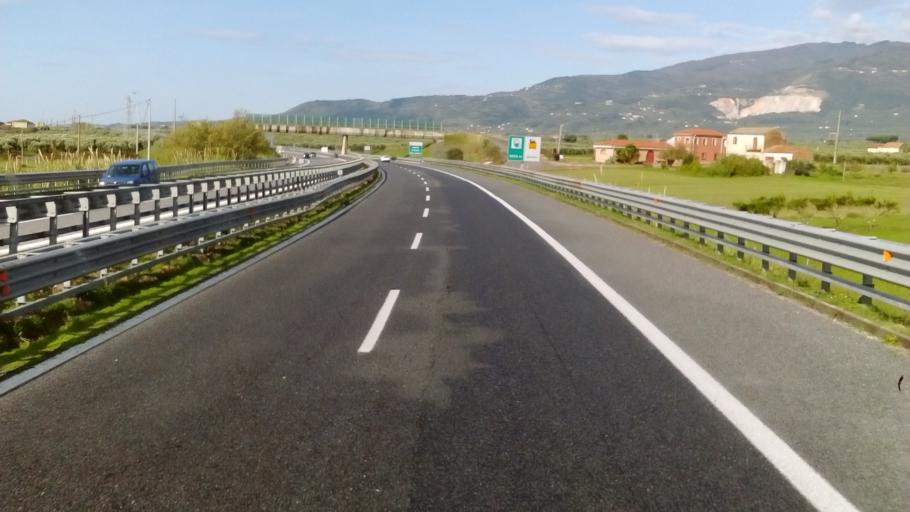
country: IT
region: Calabria
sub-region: Provincia di Catanzaro
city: Santa Eufemia Lamezia
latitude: 38.9217
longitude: 16.2619
